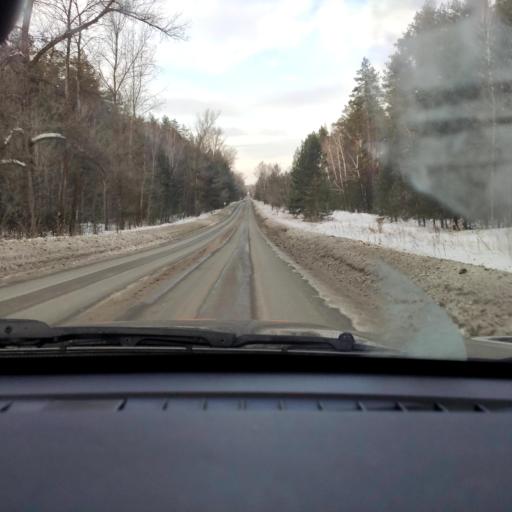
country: RU
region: Samara
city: Pribrezhnyy
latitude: 53.5019
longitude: 49.8491
